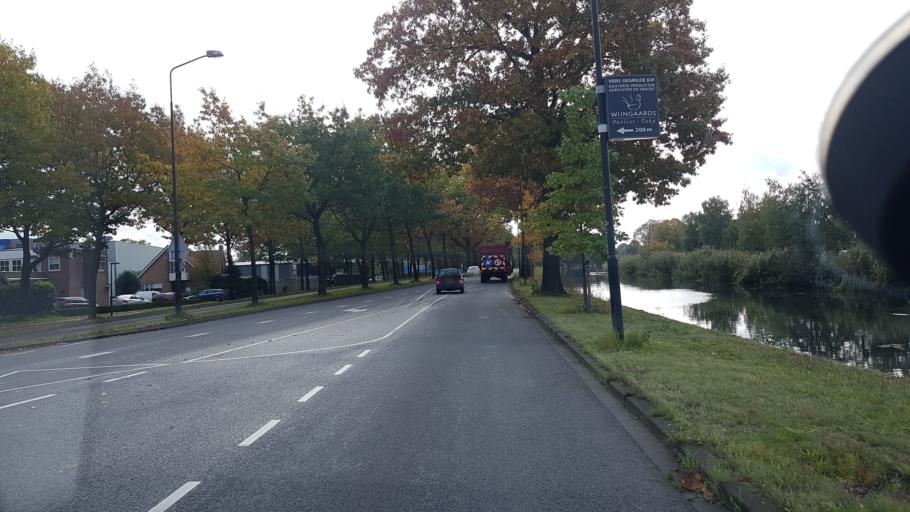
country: NL
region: Gelderland
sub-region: Gemeente Apeldoorn
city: Apeldoorn
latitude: 52.2077
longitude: 5.9790
